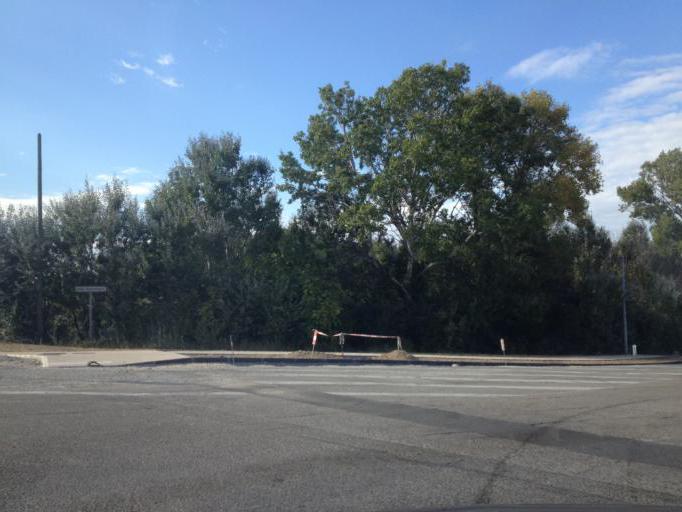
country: FR
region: Provence-Alpes-Cote d'Azur
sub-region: Departement du Vaucluse
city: Orange
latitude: 44.1223
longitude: 4.8378
